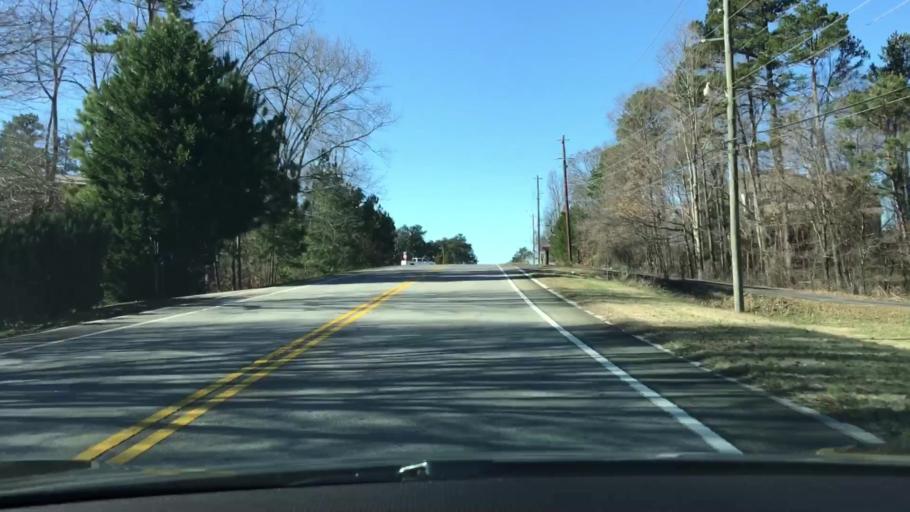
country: US
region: Georgia
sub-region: Gwinnett County
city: Buford
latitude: 34.1429
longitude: -83.9958
